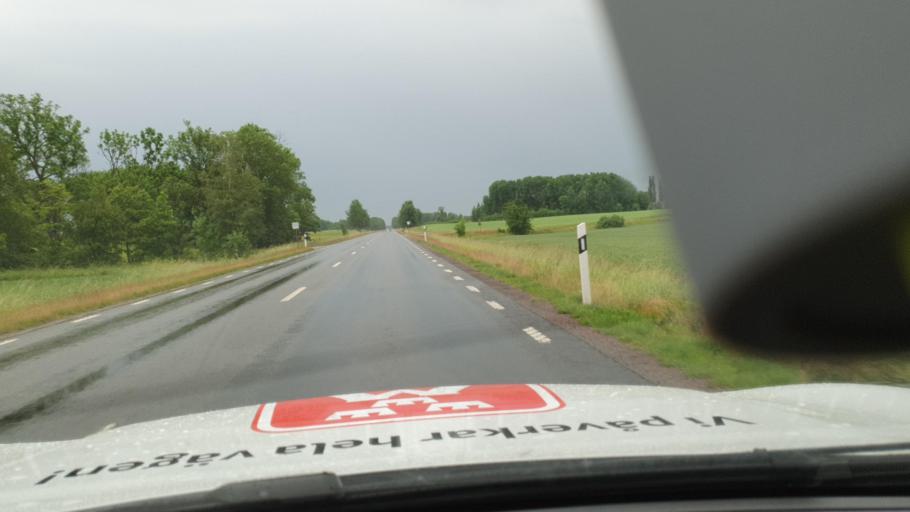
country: SE
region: Vaestra Goetaland
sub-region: Mariestads Kommun
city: Mariestad
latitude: 58.6610
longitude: 13.8813
